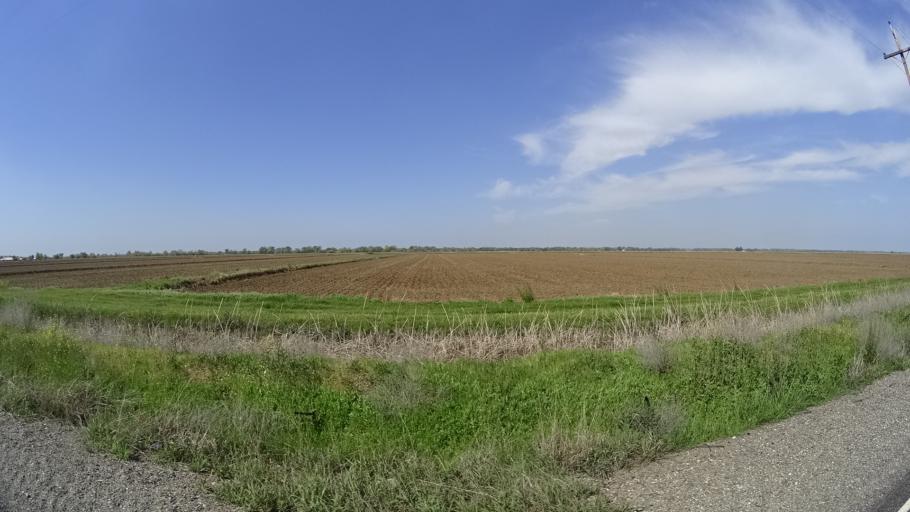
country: US
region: California
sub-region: Butte County
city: Durham
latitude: 39.5059
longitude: -121.9298
